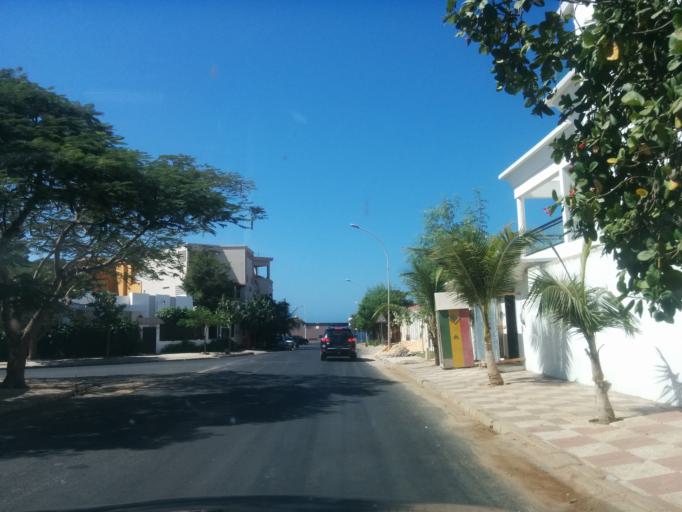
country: SN
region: Dakar
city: Mermoz Boabab
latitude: 14.7095
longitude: -17.4854
